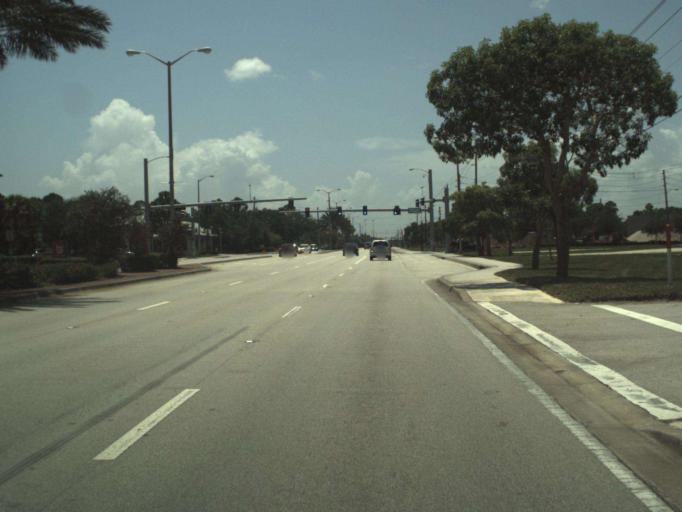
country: US
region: Florida
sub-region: Saint Lucie County
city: Port Saint Lucie
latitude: 27.2647
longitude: -80.4087
